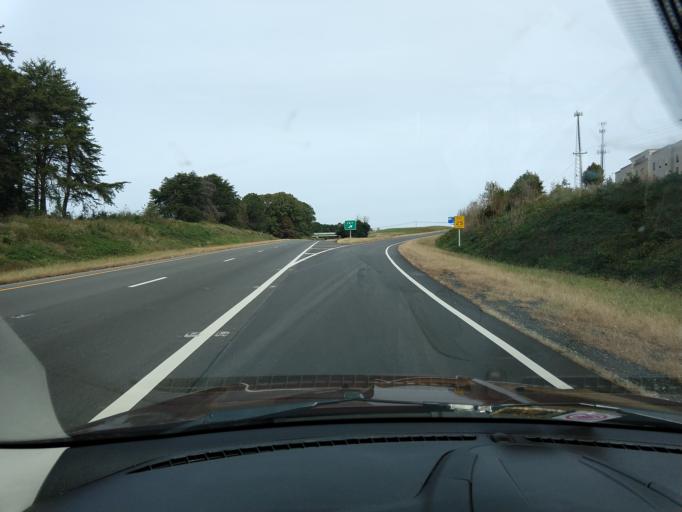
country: US
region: Virginia
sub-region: Pittsylvania County
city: Gretna
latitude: 36.9507
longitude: -79.3785
